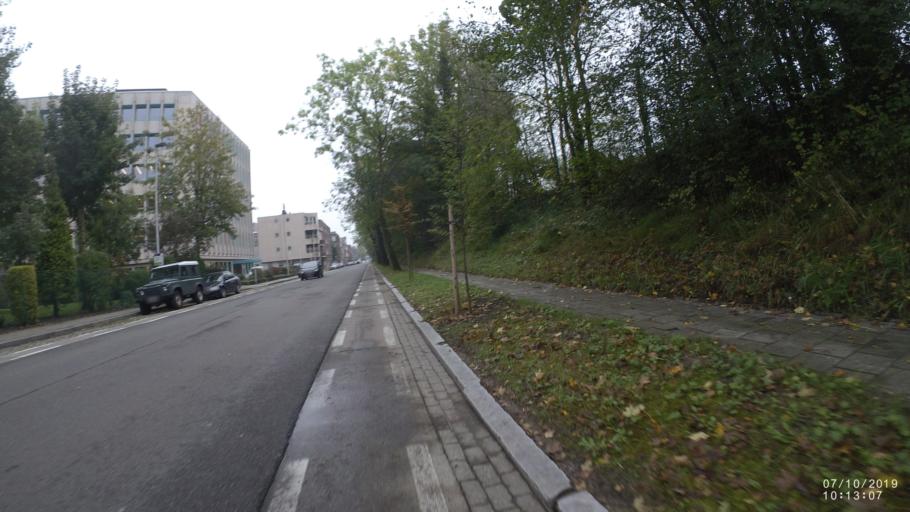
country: BE
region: Flanders
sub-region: Provincie Oost-Vlaanderen
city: Gent
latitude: 51.0395
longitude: 3.6986
